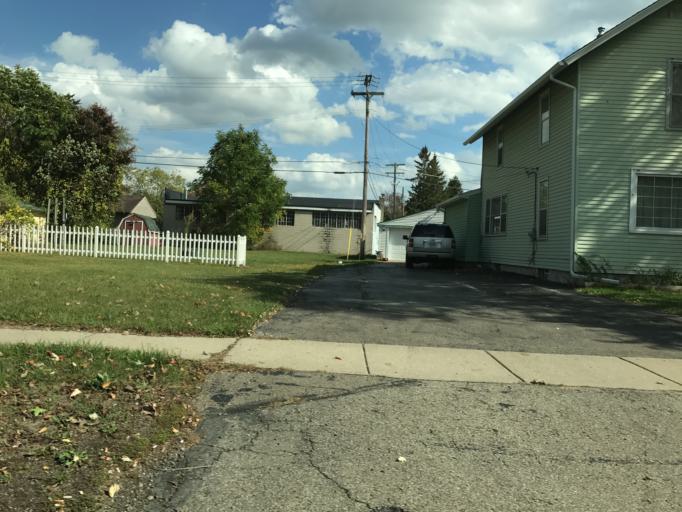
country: US
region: Michigan
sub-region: Oakland County
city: South Lyon
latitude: 42.5096
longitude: -83.6156
